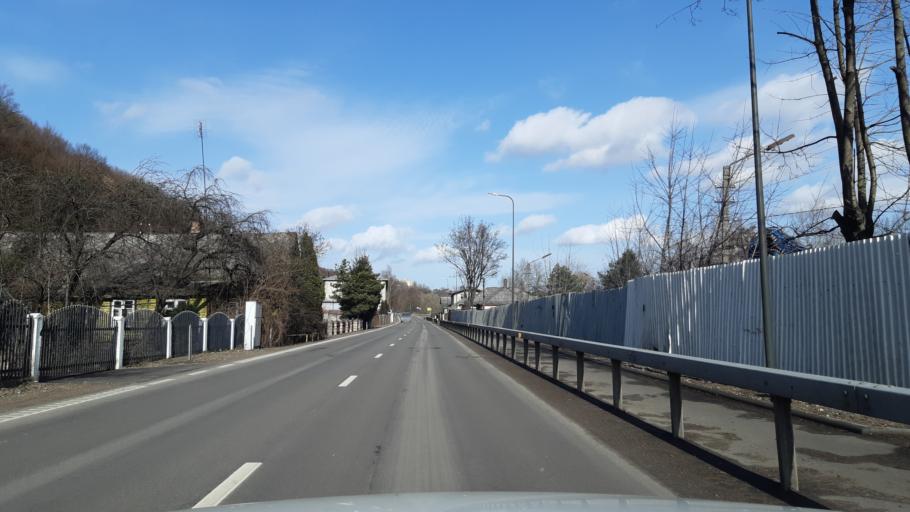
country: LT
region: Kauno apskritis
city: Dainava (Kaunas)
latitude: 54.8790
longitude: 23.9574
